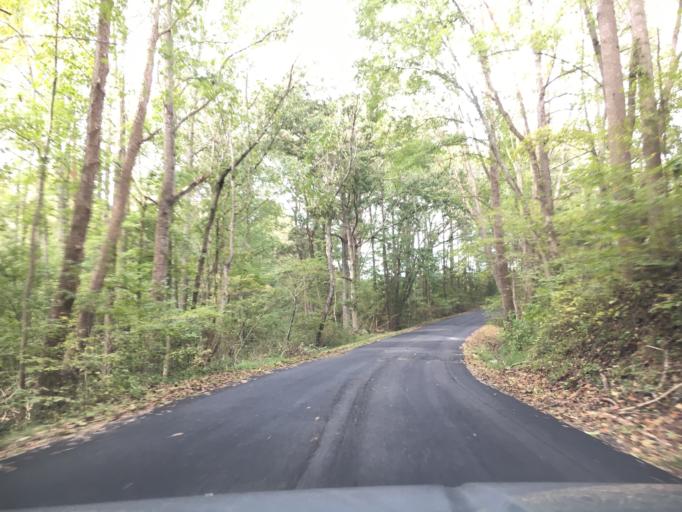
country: US
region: Virginia
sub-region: Goochland County
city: Goochland
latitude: 37.7031
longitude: -77.8381
